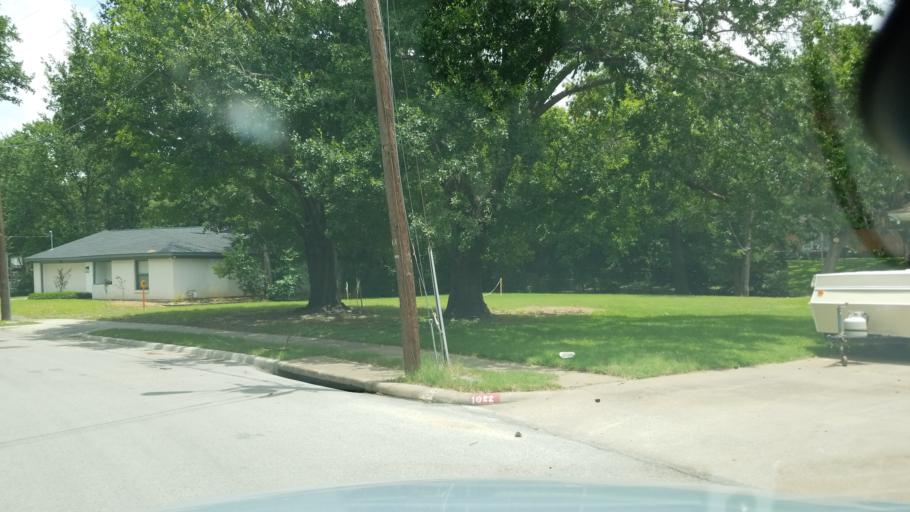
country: US
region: Texas
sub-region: Dallas County
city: Irving
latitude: 32.8248
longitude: -96.9238
